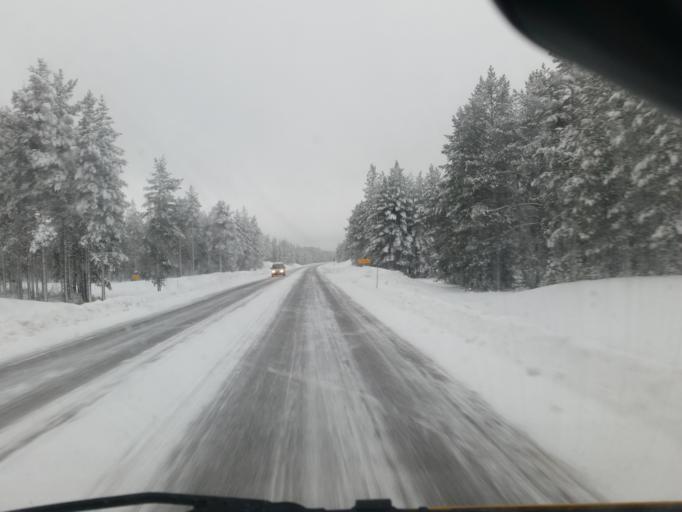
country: SE
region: Norrbotten
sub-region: Pitea Kommun
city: Pitea
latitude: 65.2505
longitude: 21.5359
